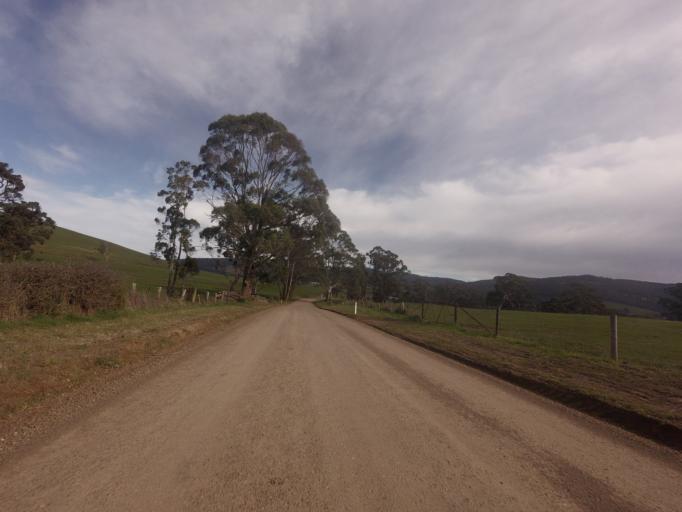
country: AU
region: Tasmania
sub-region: Huon Valley
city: Franklin
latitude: -43.0726
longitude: 147.0462
